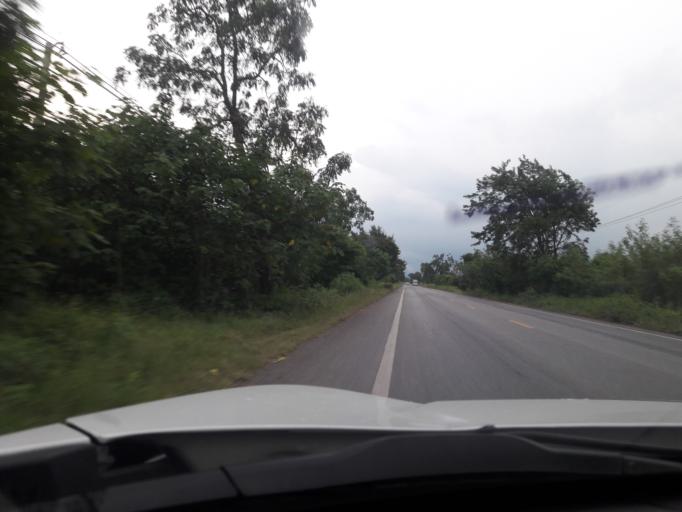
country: TH
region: Lop Buri
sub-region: Amphoe Tha Luang
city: Tha Luang
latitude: 15.0623
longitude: 101.1291
